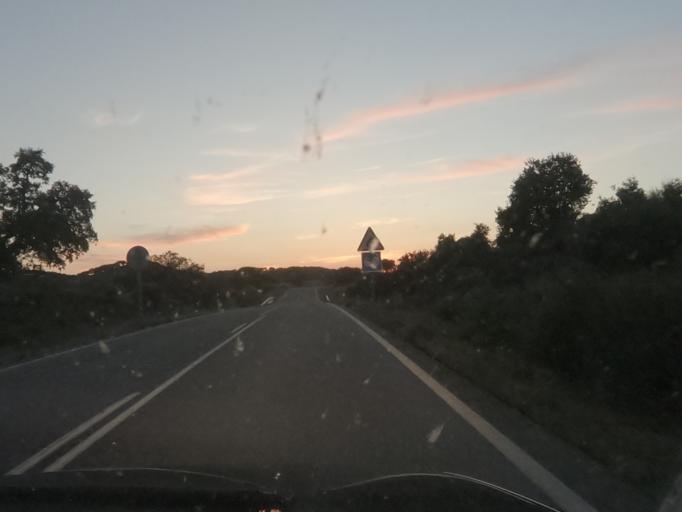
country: ES
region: Extremadura
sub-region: Provincia de Caceres
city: Piedras Albas
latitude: 39.7881
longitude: -6.9550
